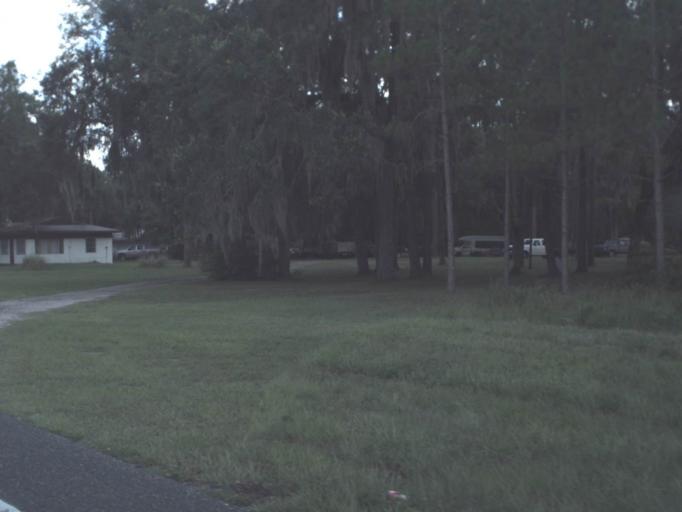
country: US
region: Florida
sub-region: Taylor County
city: Perry
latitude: 30.0338
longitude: -83.5438
